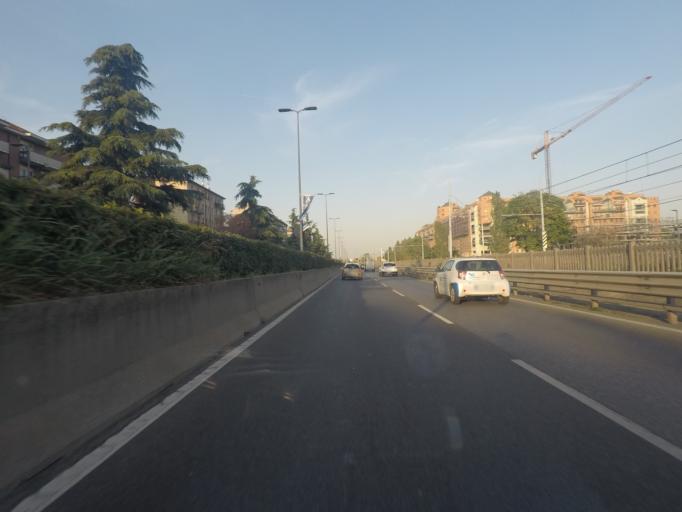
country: IT
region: Lombardy
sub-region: Citta metropolitana di Milano
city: Sesto San Giovanni
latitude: 45.5073
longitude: 9.2507
